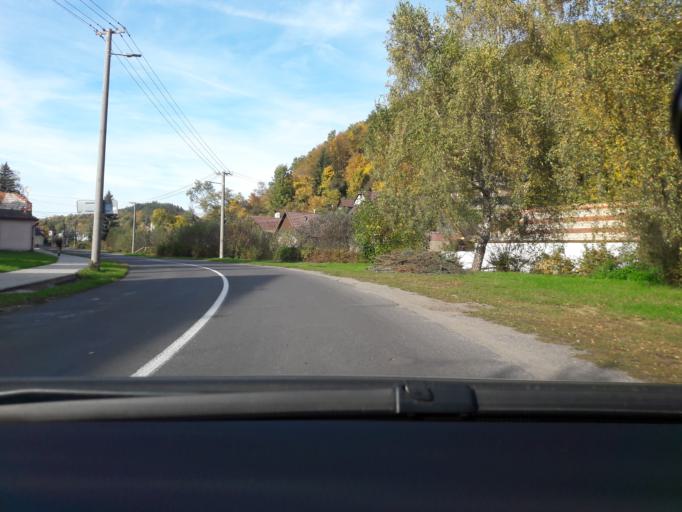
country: SK
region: Banskobystricky
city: Svaety Anton
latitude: 48.4228
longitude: 18.9409
